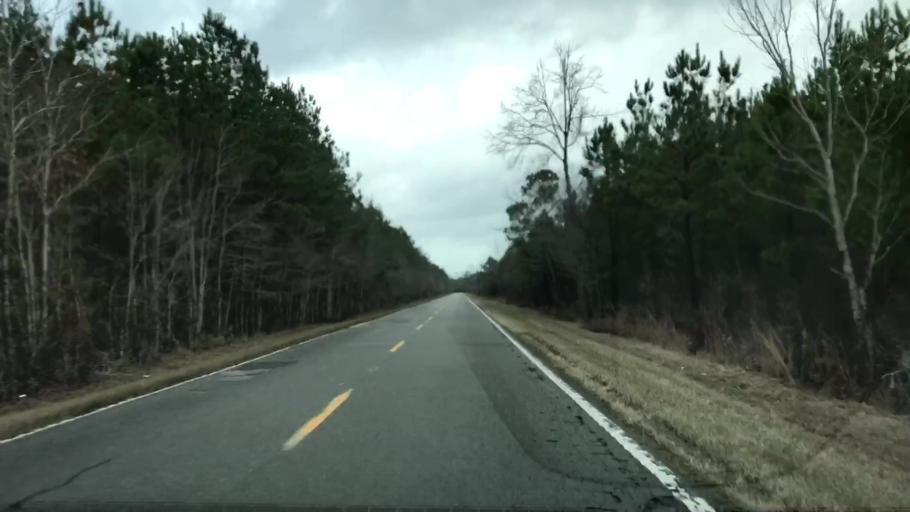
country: US
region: South Carolina
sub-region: Georgetown County
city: Murrells Inlet
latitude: 33.6276
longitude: -79.2434
